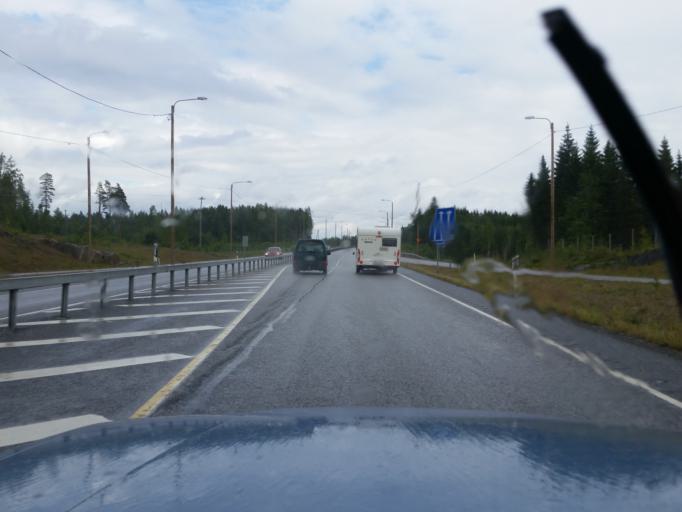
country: FI
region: Southern Savonia
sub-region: Mikkeli
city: Pertunmaa
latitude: 61.4338
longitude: 26.6030
